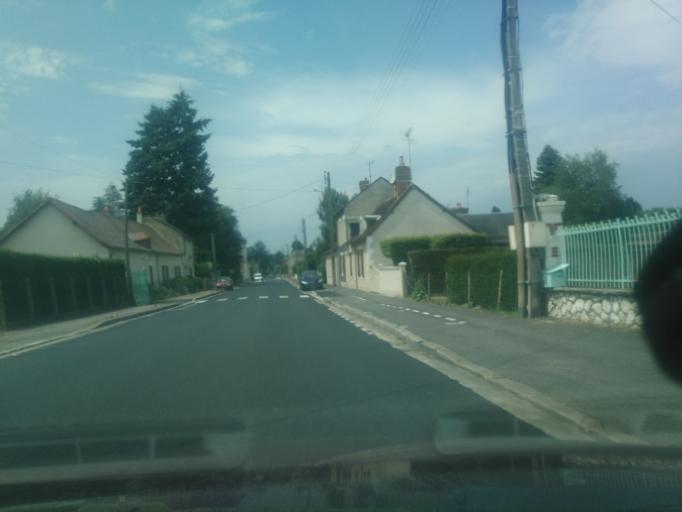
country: FR
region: Centre
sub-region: Departement de l'Indre
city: Le Blanc
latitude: 46.6282
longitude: 1.0753
